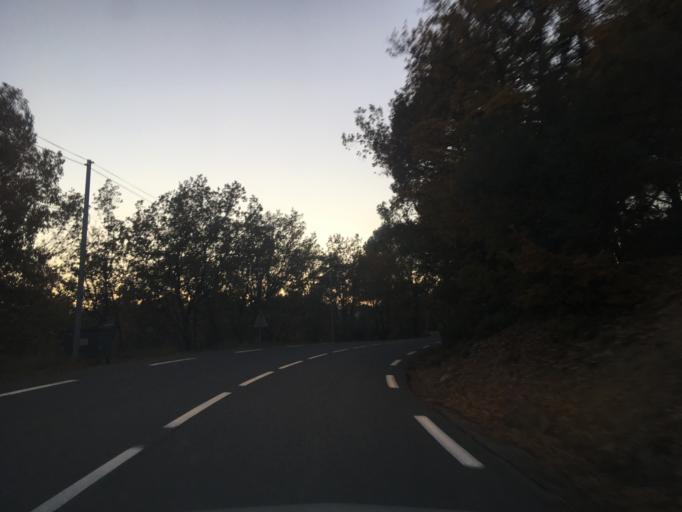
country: FR
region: Provence-Alpes-Cote d'Azur
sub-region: Departement du Var
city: Figanieres
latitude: 43.5459
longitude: 6.5285
